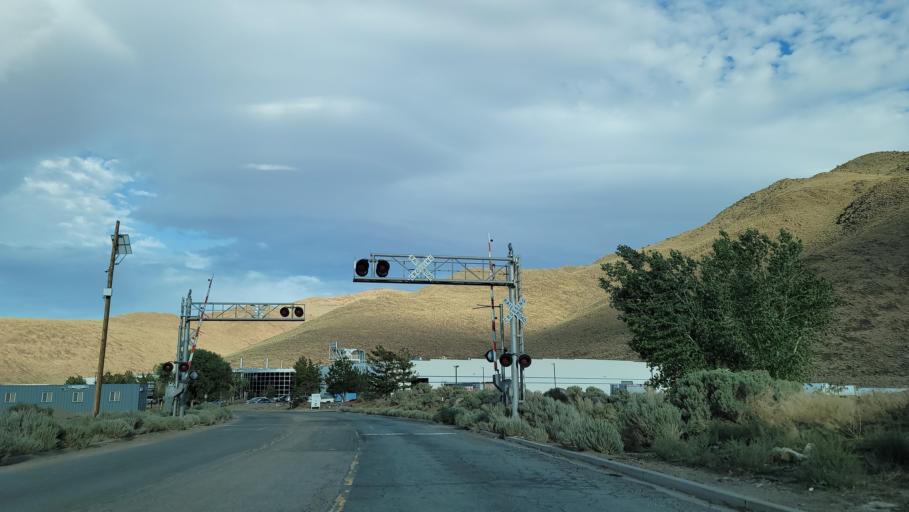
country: US
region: Nevada
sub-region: Washoe County
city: Spanish Springs
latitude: 39.5491
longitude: -119.5482
